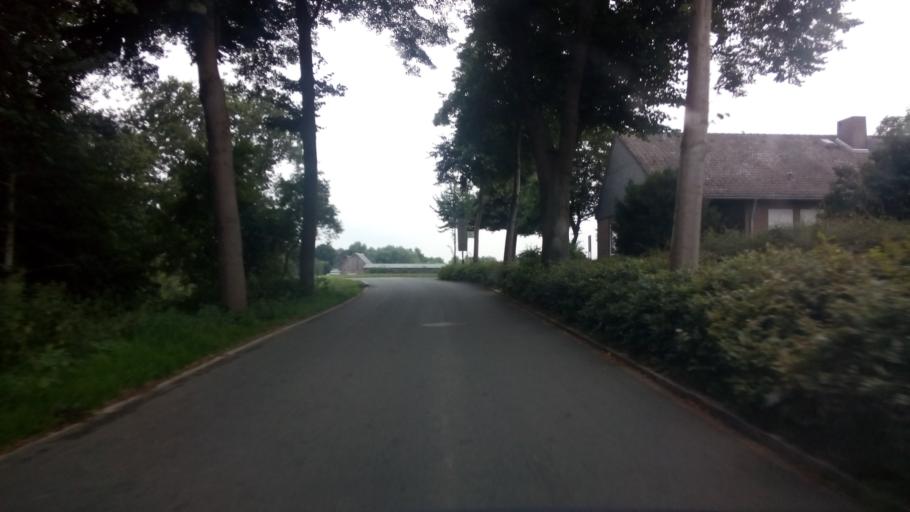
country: DE
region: Lower Saxony
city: Lilienthal
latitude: 53.1276
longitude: 8.8708
